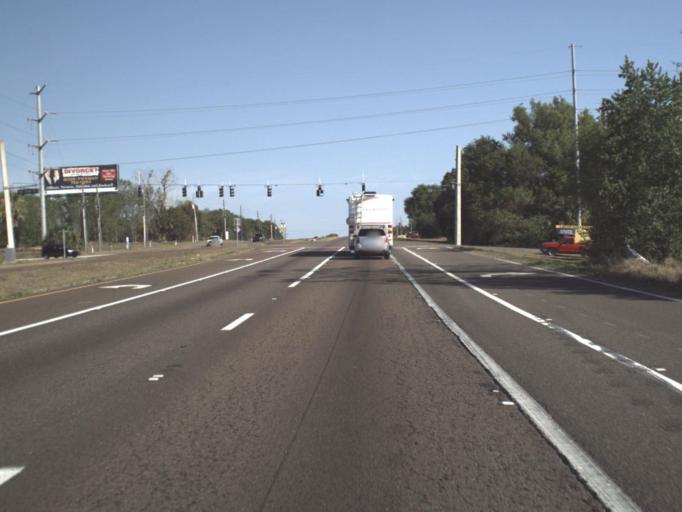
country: US
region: Florida
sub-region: Lake County
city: Minneola
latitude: 28.6004
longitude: -81.7546
